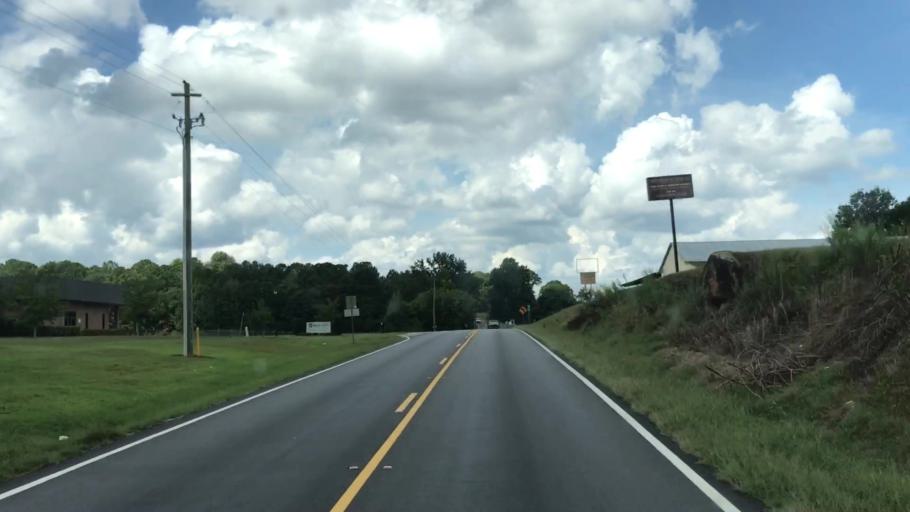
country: US
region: Georgia
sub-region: Greene County
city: Greensboro
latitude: 33.5700
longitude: -83.1648
